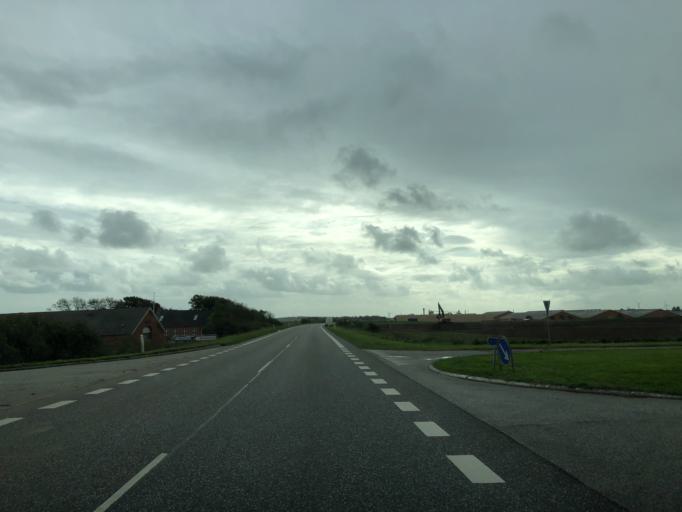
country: DK
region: North Denmark
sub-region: Thisted Kommune
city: Hurup
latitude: 56.7527
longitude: 8.4469
